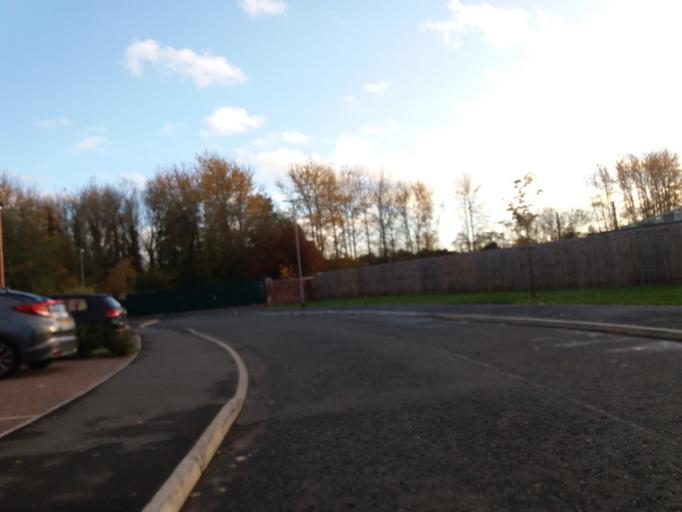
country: GB
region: England
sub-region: Lancashire
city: Euxton
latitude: 53.6676
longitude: -2.6469
